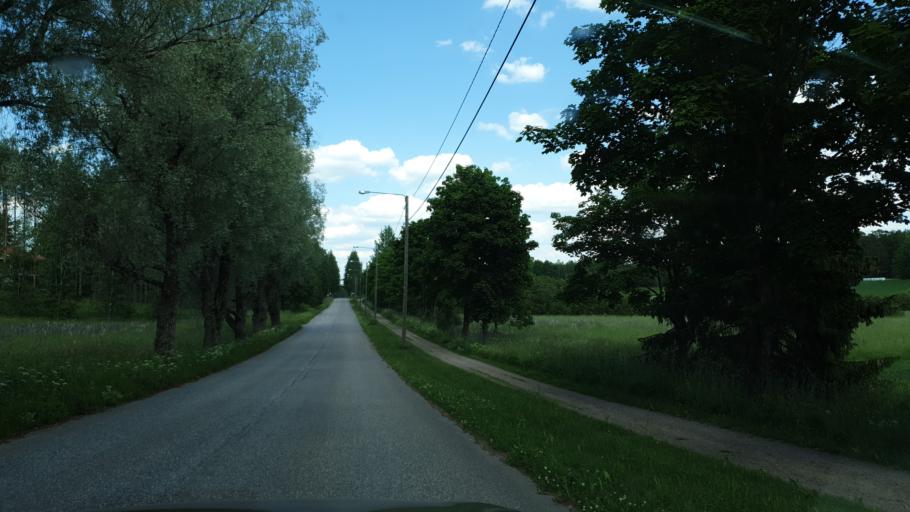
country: FI
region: Uusimaa
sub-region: Helsinki
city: Vihti
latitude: 60.3773
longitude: 24.5093
